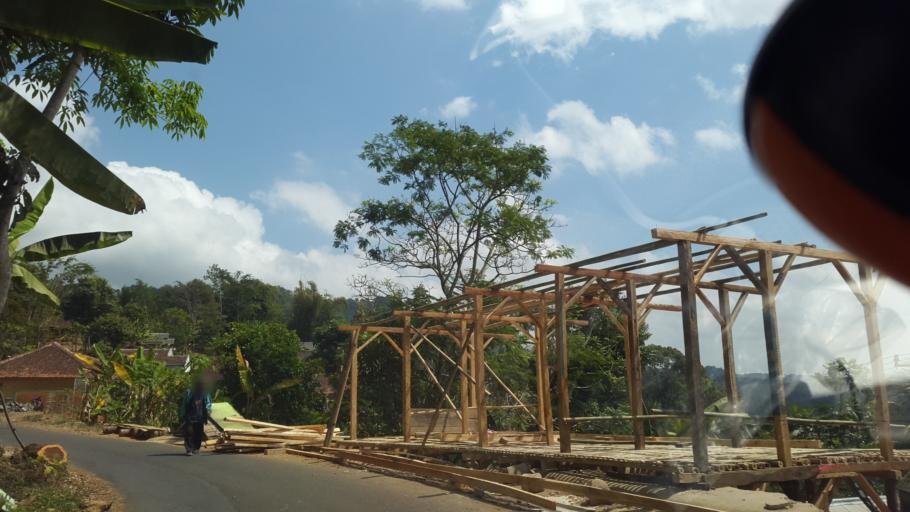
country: ID
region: West Java
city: Cidadap
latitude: -7.2775
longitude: 106.9346
